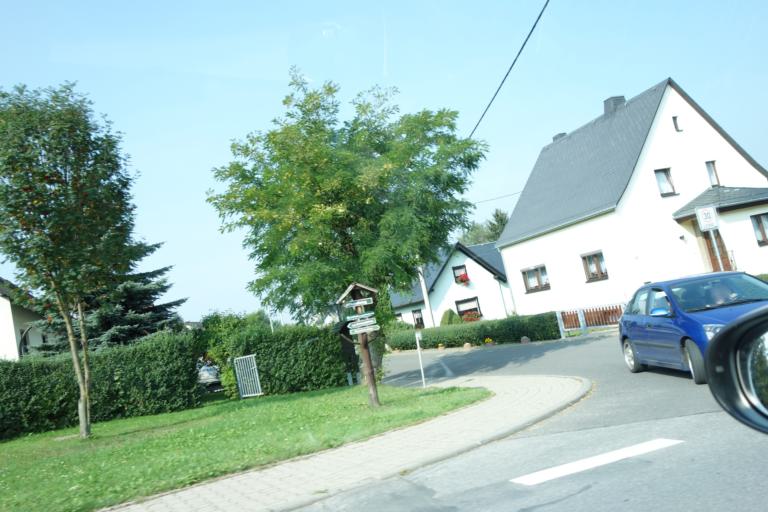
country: DE
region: Saxony
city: Bornichen
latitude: 50.7658
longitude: 13.1478
